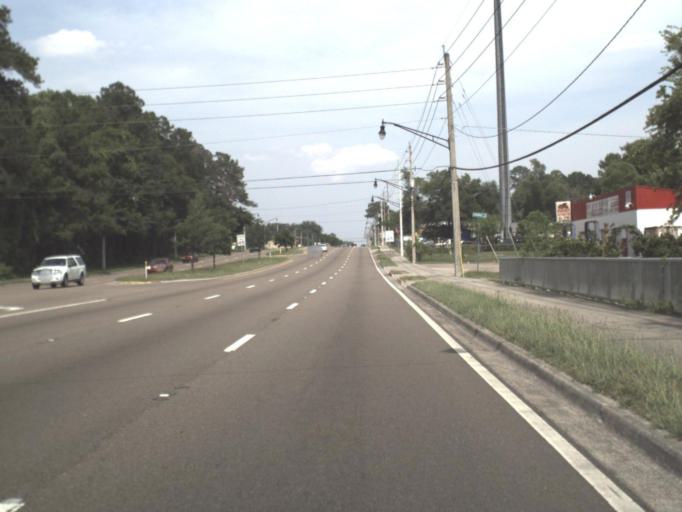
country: US
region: Florida
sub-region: Clay County
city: Bellair-Meadowbrook Terrace
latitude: 30.2476
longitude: -81.7965
